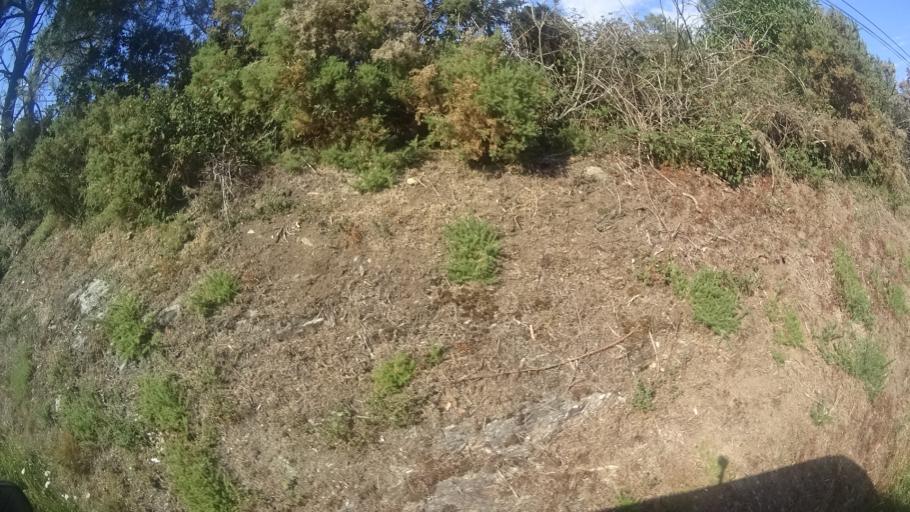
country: FR
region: Brittany
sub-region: Departement du Morbihan
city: Beganne
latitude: 47.5810
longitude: -2.2846
